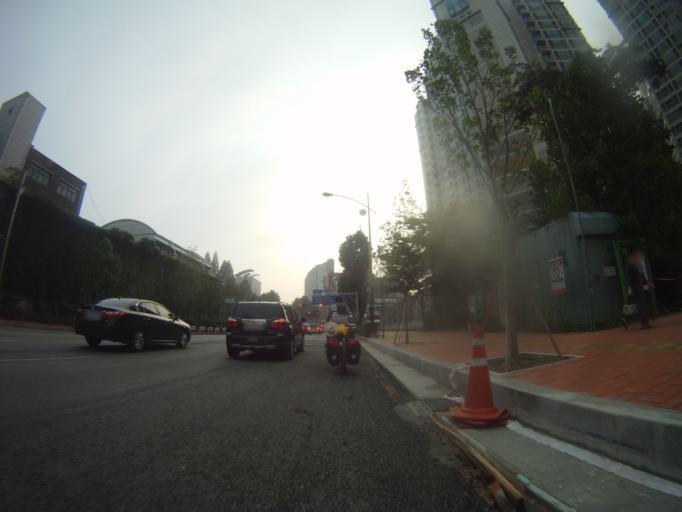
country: KR
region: Incheon
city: Incheon
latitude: 37.4568
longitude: 126.7060
